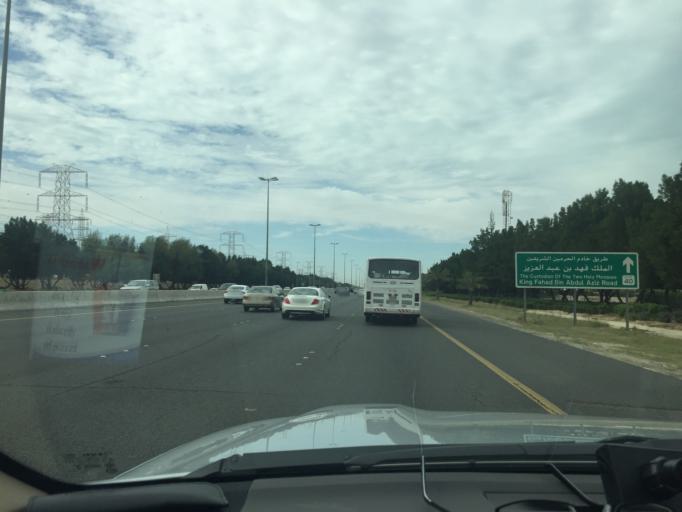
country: KW
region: Mubarak al Kabir
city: Sabah as Salim
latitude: 29.2463
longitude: 48.0481
